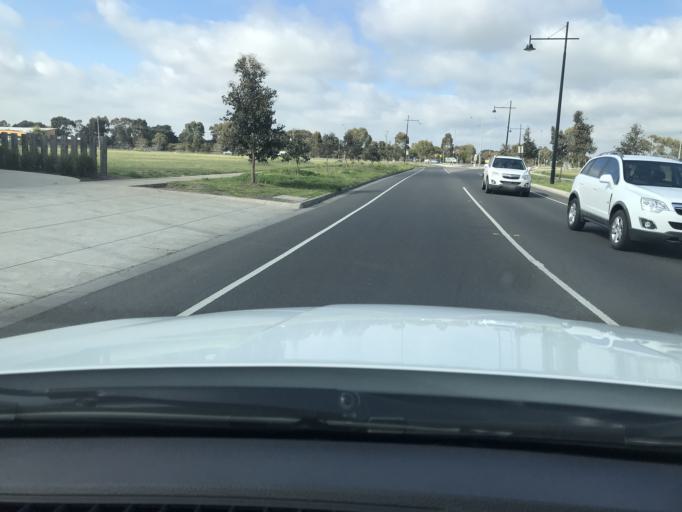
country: AU
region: Victoria
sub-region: Hume
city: Roxburgh Park
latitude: -37.5944
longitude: 144.9178
